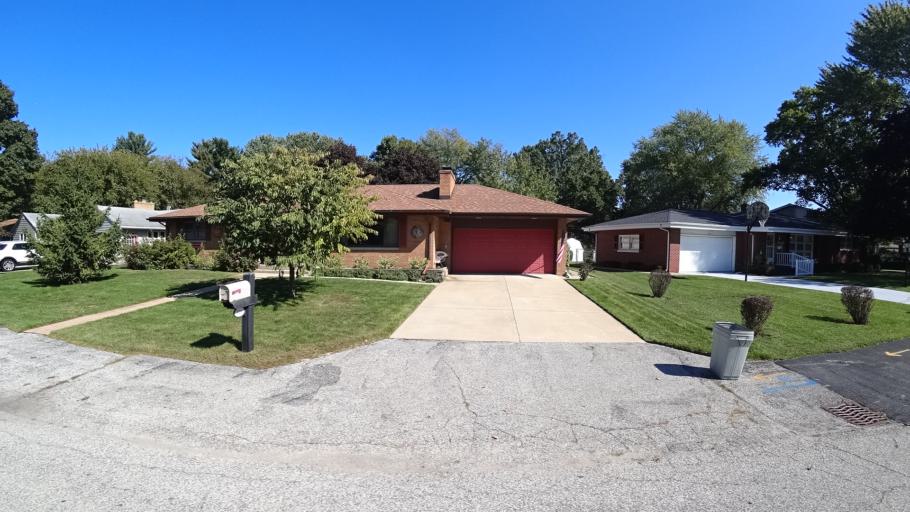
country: US
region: Indiana
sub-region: LaPorte County
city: Michigan City
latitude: 41.6893
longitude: -86.8924
